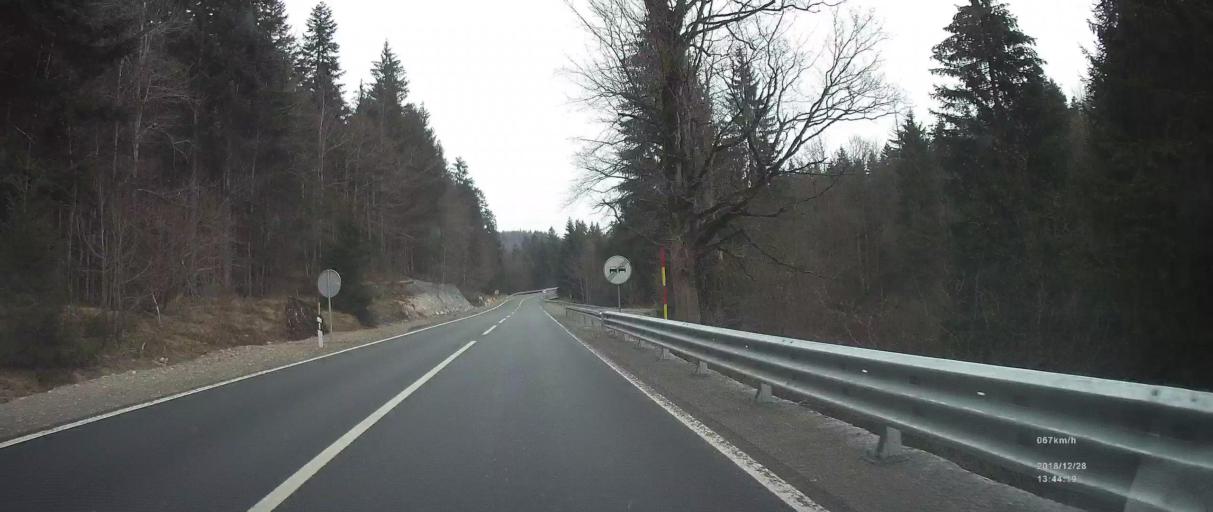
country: HR
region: Primorsko-Goranska
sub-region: Grad Delnice
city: Delnice
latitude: 45.3725
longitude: 14.7817
